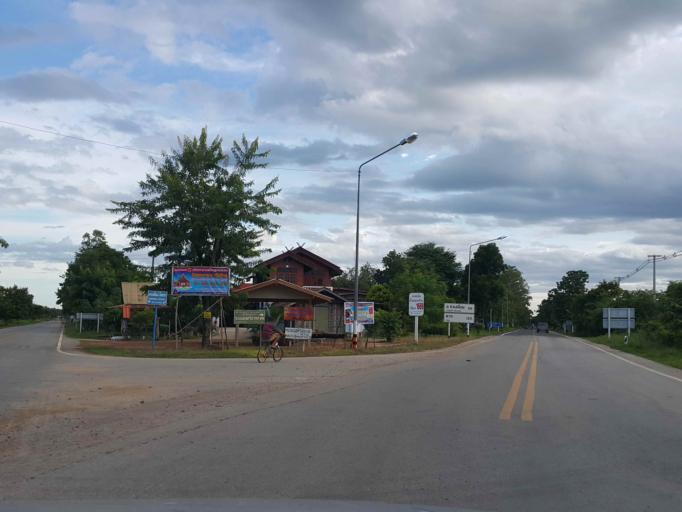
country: TH
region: Sukhothai
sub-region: Amphoe Si Satchanalai
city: Si Satchanalai
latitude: 17.4979
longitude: 99.7526
